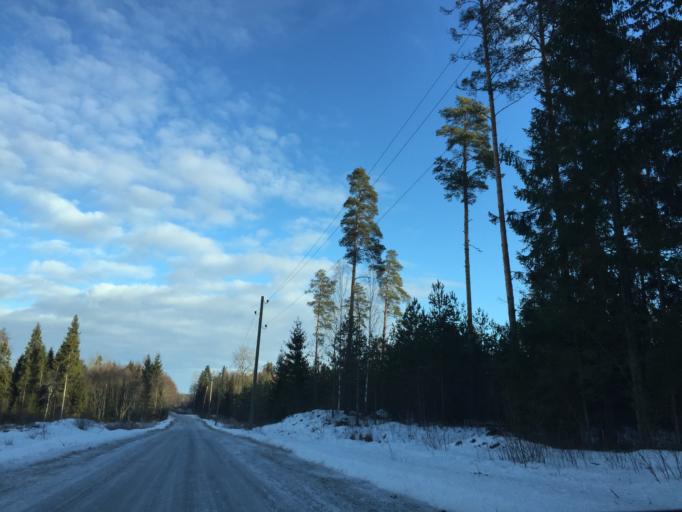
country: LV
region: Kegums
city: Kegums
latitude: 56.7362
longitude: 24.6643
